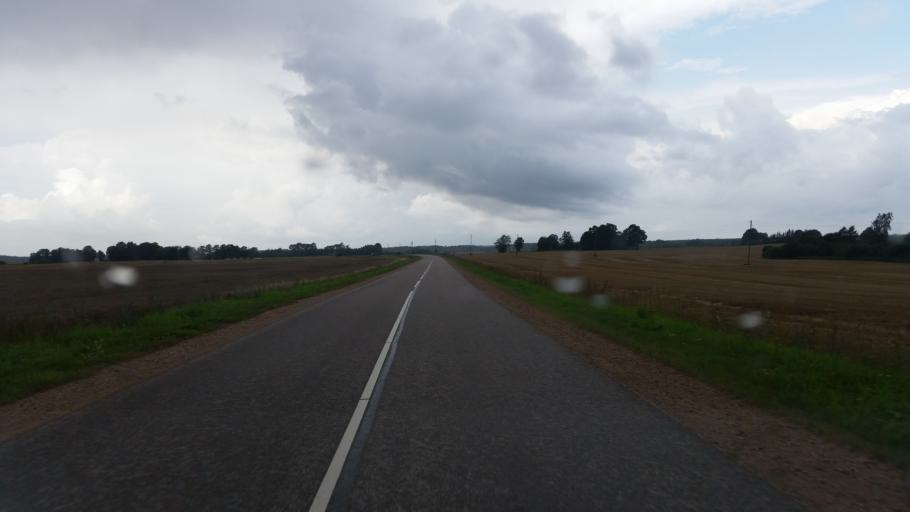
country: LV
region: Vecumnieki
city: Vecumnieki
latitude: 56.4328
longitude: 24.4339
